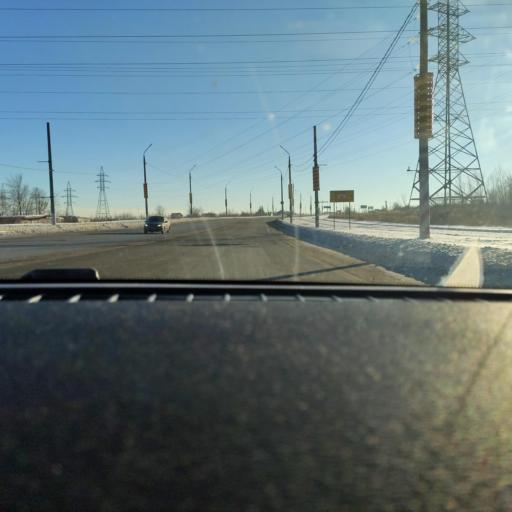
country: RU
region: Samara
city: Novokuybyshevsk
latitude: 53.0848
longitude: 49.9985
